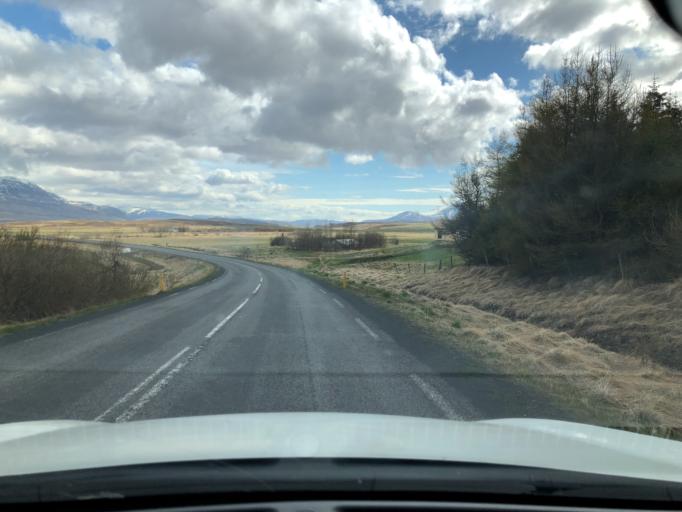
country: IS
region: Northwest
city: Saudarkrokur
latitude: 65.5462
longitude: -19.4744
